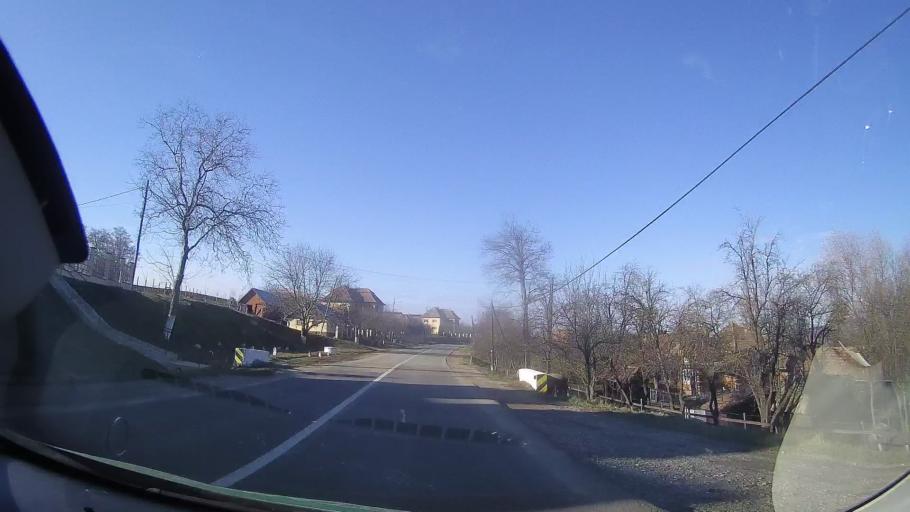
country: RO
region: Cluj
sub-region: Comuna Mociu
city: Mociu
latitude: 46.7909
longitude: 24.0730
